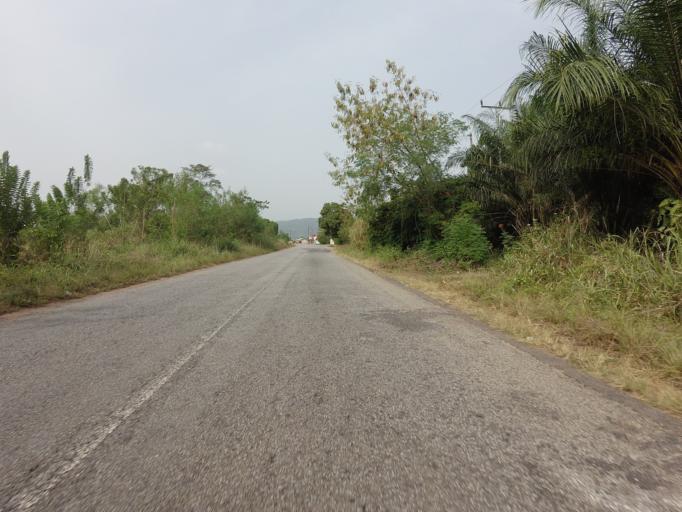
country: GH
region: Volta
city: Ho
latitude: 6.5756
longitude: 0.3356
